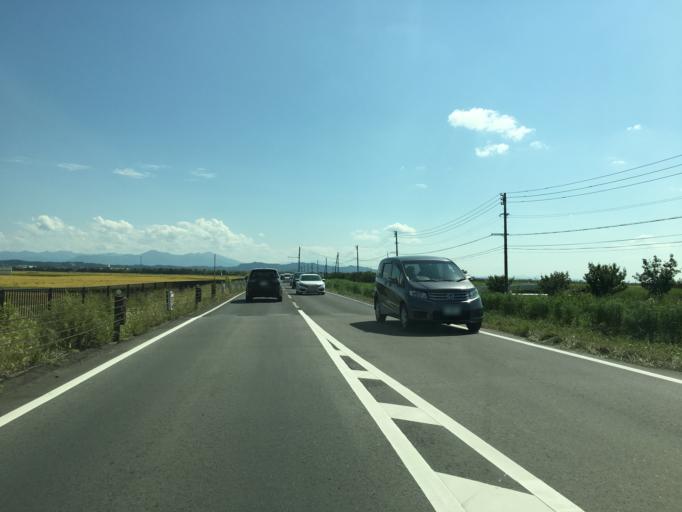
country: JP
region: Niigata
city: Niitsu-honcho
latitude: 37.8315
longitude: 139.0970
